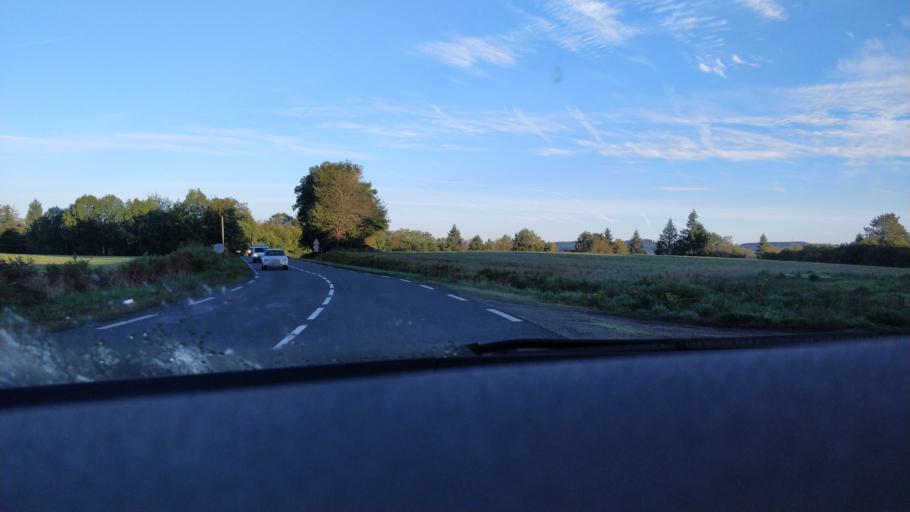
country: FR
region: Limousin
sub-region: Departement de la Haute-Vienne
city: Sauviat-sur-Vige
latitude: 45.9329
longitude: 1.6522
